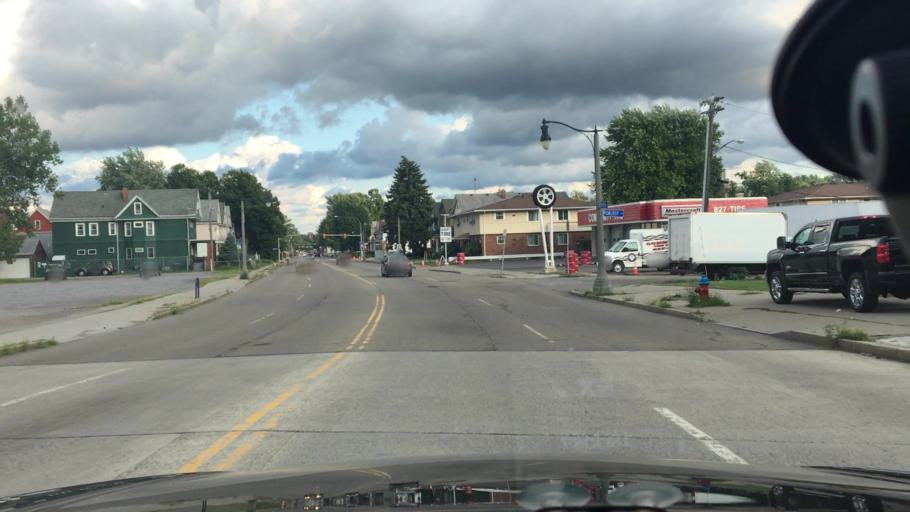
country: US
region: New York
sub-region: Erie County
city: West Seneca
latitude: 42.8635
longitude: -78.8210
